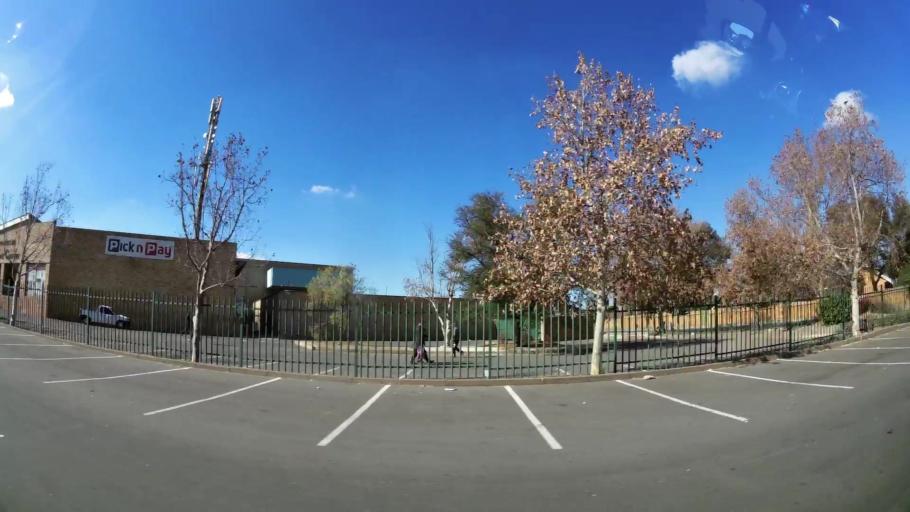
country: ZA
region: Gauteng
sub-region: City of Johannesburg Metropolitan Municipality
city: Roodepoort
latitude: -26.1410
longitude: 27.8306
